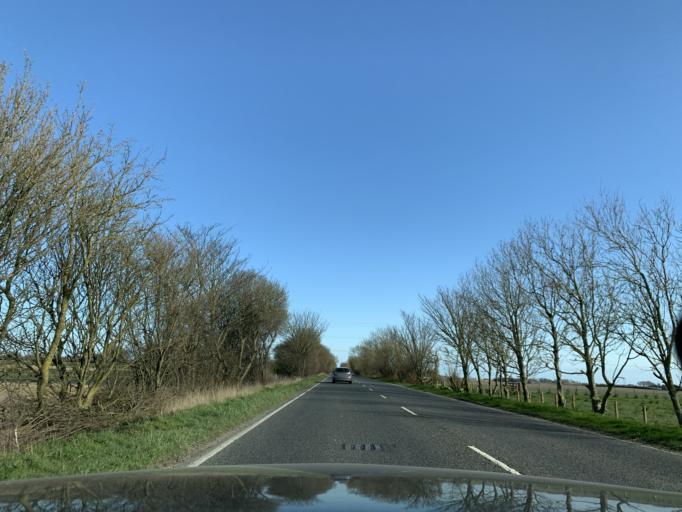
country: GB
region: England
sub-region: Kent
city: New Romney
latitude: 50.9874
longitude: 0.9079
